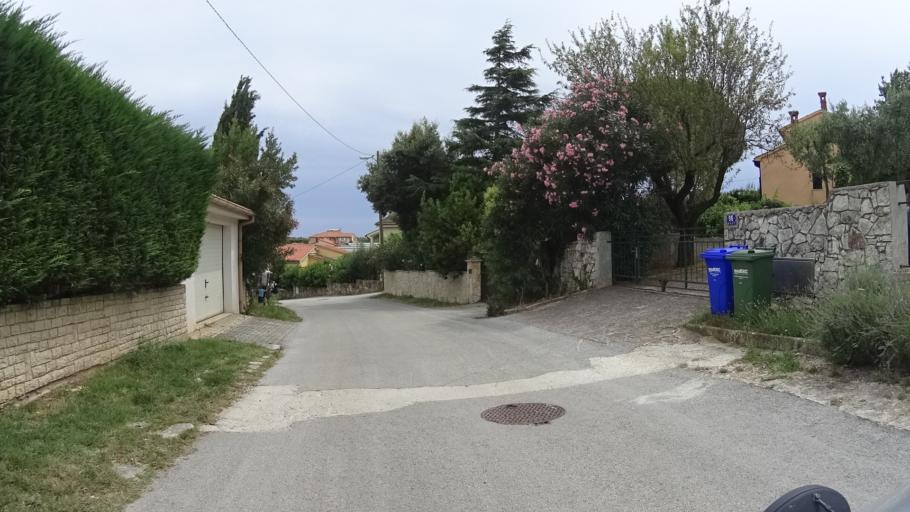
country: HR
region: Istarska
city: Medulin
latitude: 44.8020
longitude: 13.9123
